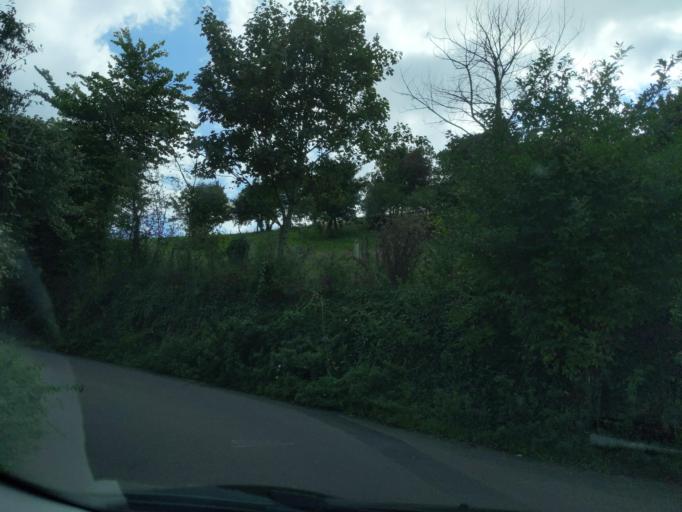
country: GB
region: England
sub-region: Plymouth
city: Plymstock
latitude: 50.3503
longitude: -4.1100
